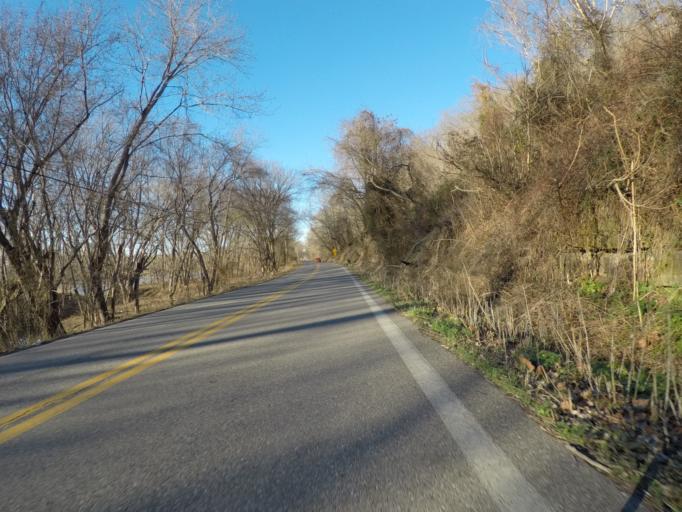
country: US
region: West Virginia
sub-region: Wayne County
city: Kenova
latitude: 38.3756
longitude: -82.5904
